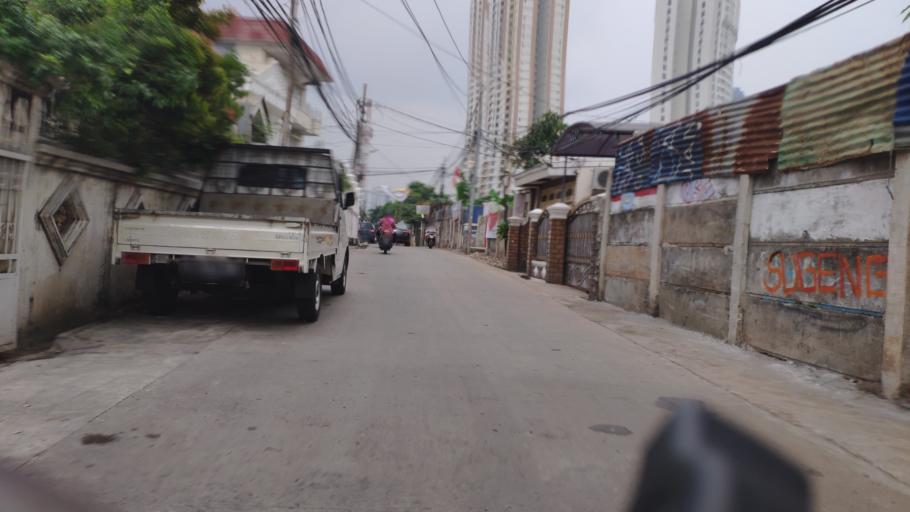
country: ID
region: Jakarta Raya
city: Jakarta
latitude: -6.2115
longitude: 106.8380
